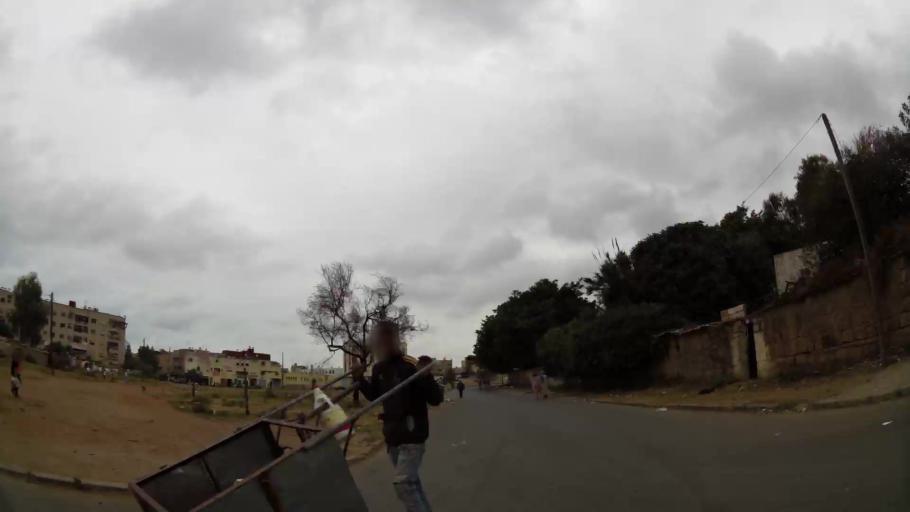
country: MA
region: Rabat-Sale-Zemmour-Zaer
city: Sale
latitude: 34.0423
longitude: -6.8031
